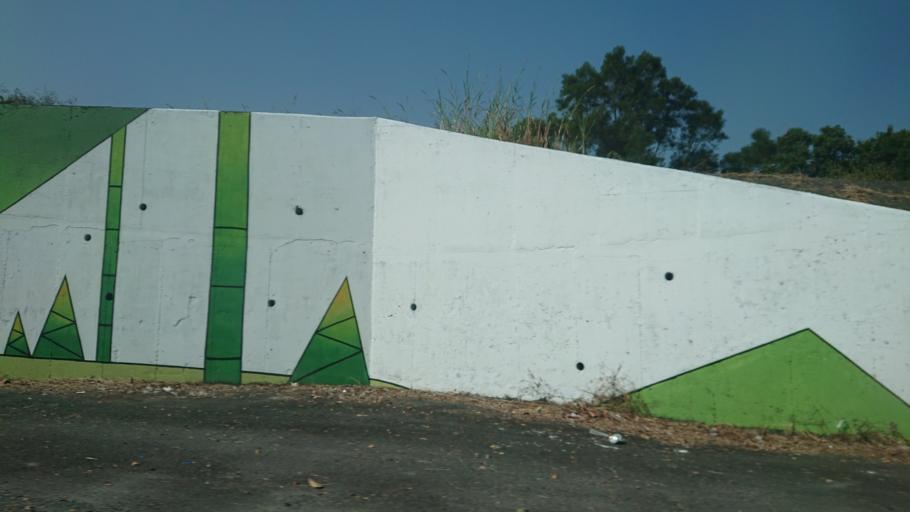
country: TW
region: Taiwan
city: Lugu
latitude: 23.7504
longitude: 120.6588
